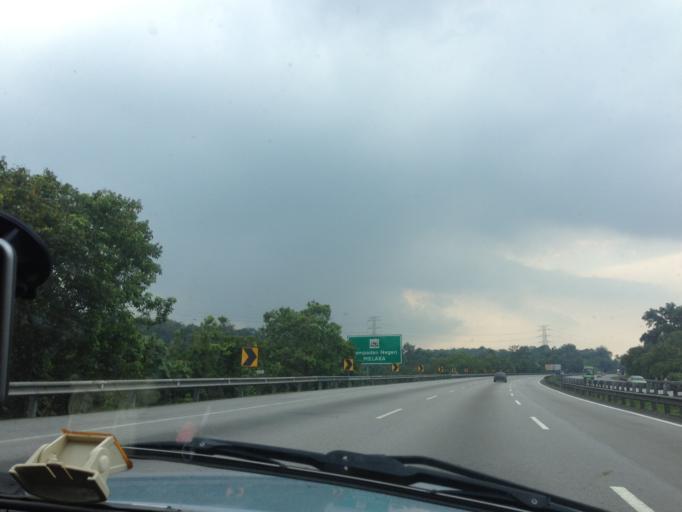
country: MY
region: Negeri Sembilan
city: Tampin
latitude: 2.4667
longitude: 102.1482
